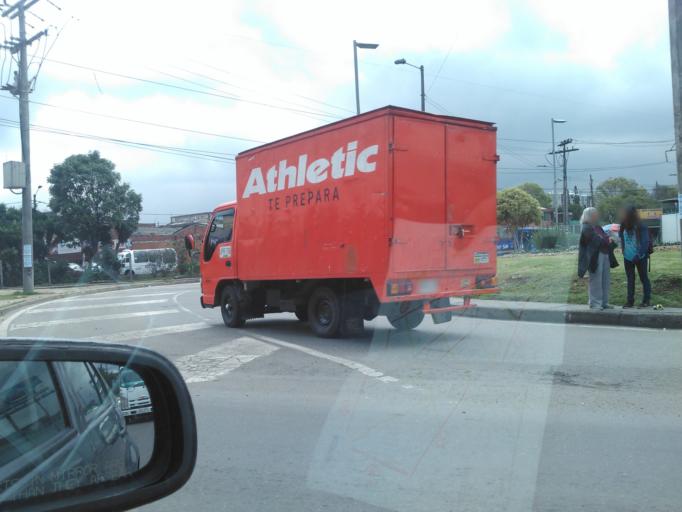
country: CO
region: Bogota D.C.
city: Bogota
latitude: 4.6238
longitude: -74.1243
